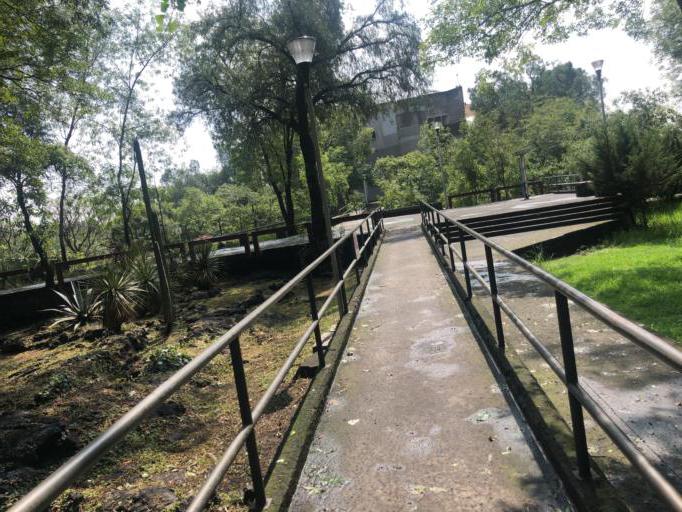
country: MX
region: Mexico City
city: Tlalpan
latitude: 19.3140
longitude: -99.1843
